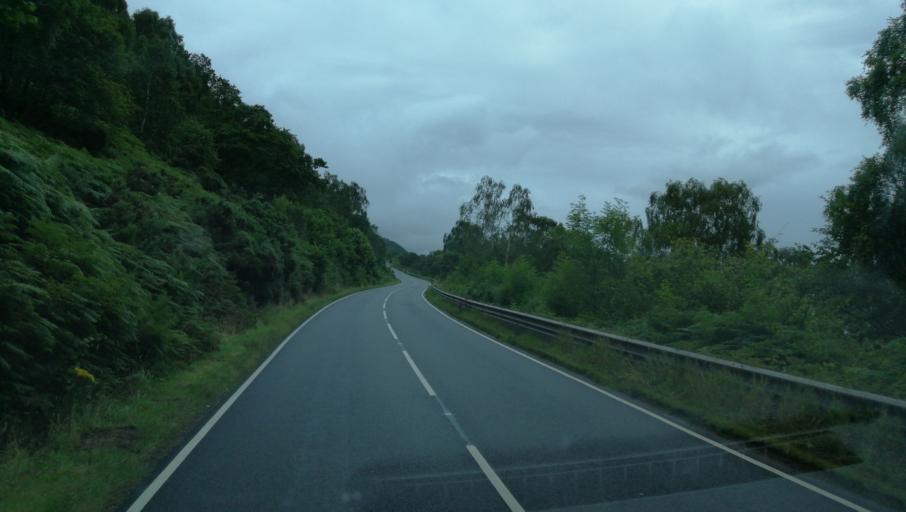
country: GB
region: Scotland
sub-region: Highland
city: Beauly
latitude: 57.3859
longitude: -4.3709
